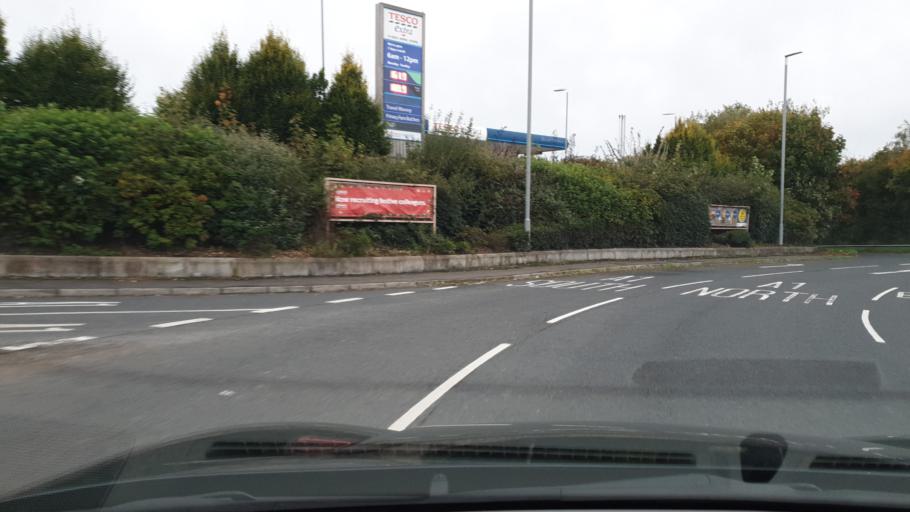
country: GB
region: Northern Ireland
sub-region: Banbridge District
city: Banbridge
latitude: 54.3299
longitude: -6.2826
